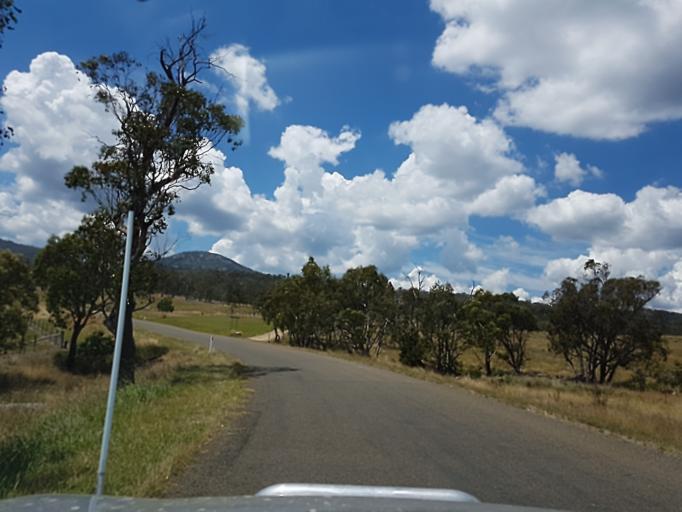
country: AU
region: Victoria
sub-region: Alpine
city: Mount Beauty
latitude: -36.9011
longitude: 147.8626
